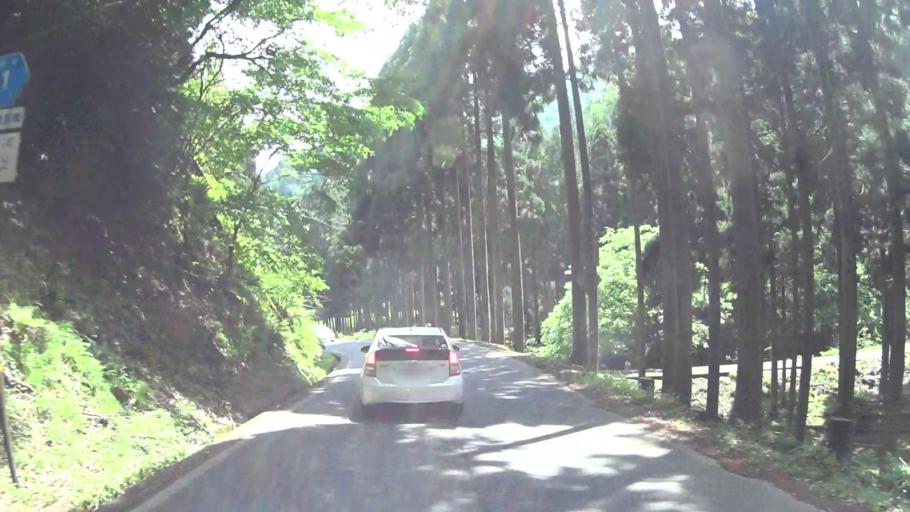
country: JP
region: Kyoto
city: Maizuru
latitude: 35.4424
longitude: 135.5104
